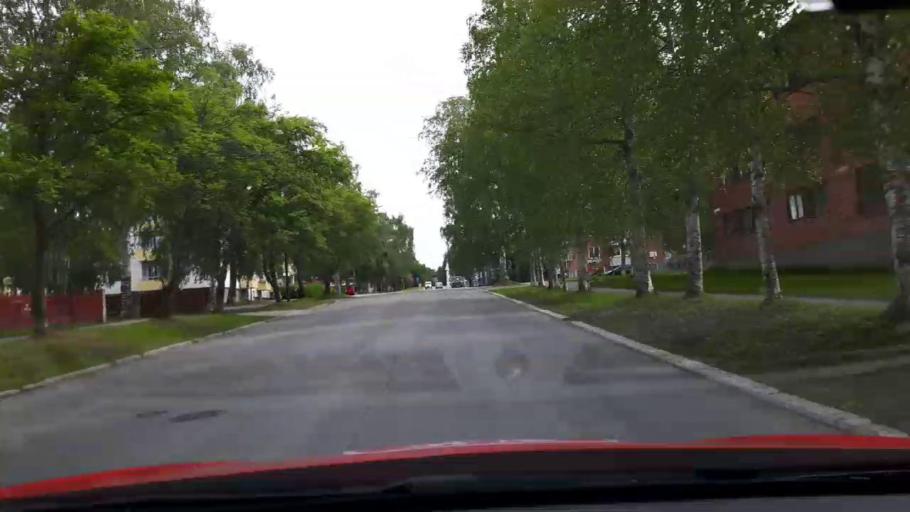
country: SE
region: Jaemtland
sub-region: OEstersunds Kommun
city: Ostersund
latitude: 63.1429
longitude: 14.4725
